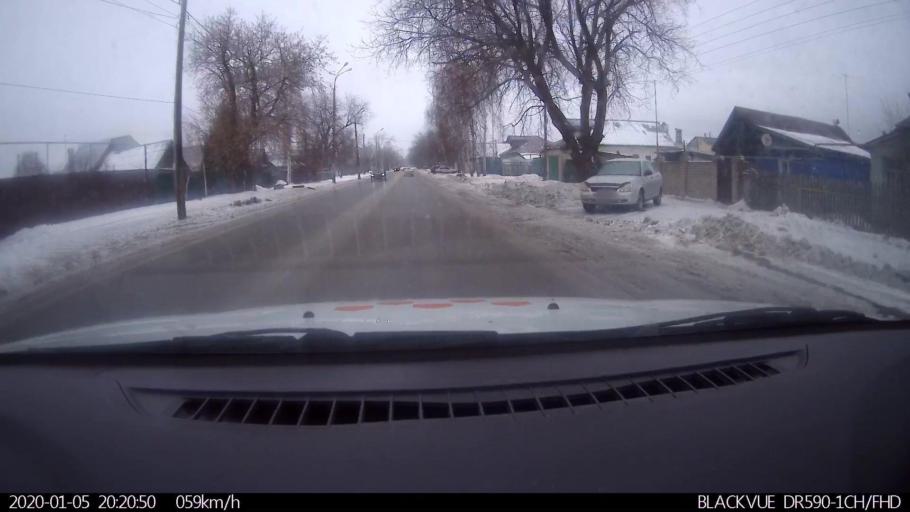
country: RU
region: Nizjnij Novgorod
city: Gorbatovka
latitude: 56.3706
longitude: 43.8110
